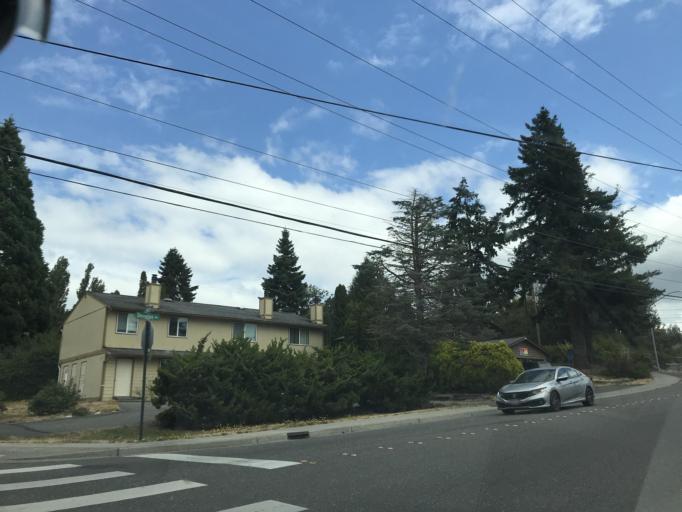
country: US
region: Washington
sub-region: Whatcom County
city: Bellingham
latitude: 48.7238
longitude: -122.4862
